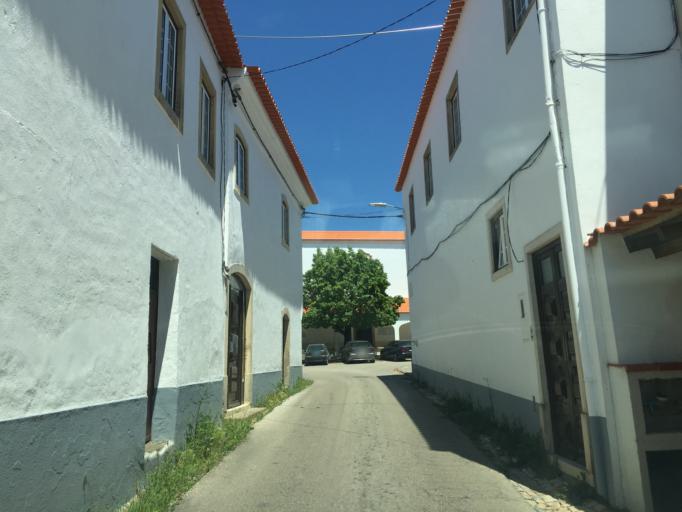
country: PT
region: Santarem
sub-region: Ferreira do Zezere
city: Ferreira do Zezere
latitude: 39.5995
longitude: -8.3009
